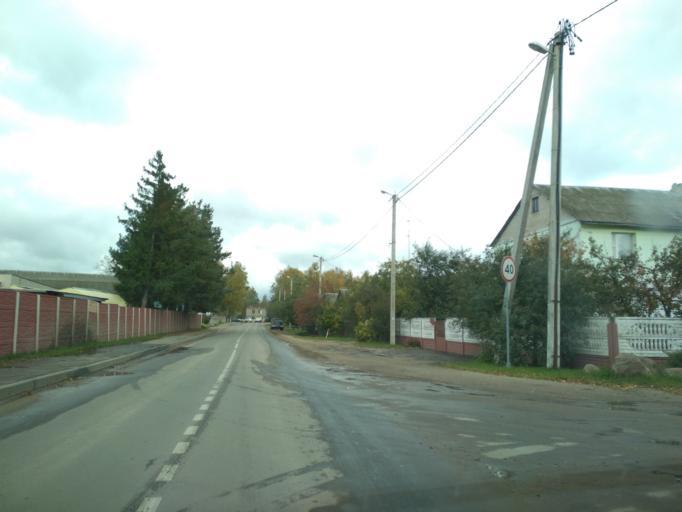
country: BY
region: Minsk
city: Mar''ina Horka
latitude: 53.5145
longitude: 28.1548
